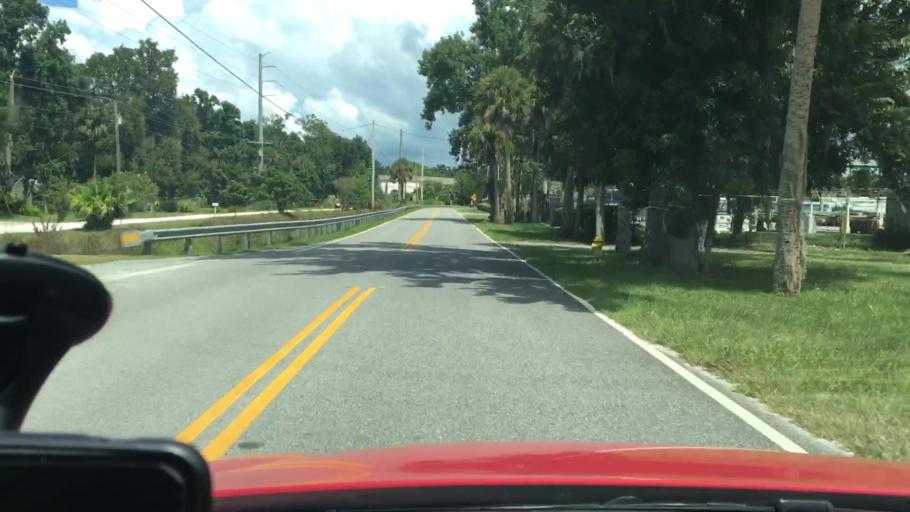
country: US
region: Florida
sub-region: Volusia County
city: Port Orange
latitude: 29.1400
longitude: -81.0007
